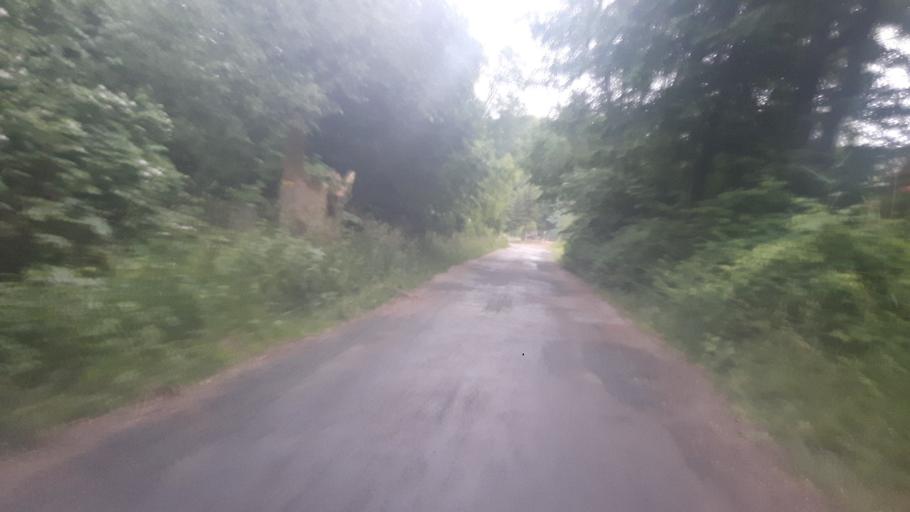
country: PL
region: Pomeranian Voivodeship
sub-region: Powiat nowodworski
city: Krynica Morska
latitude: 54.2830
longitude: 19.4317
